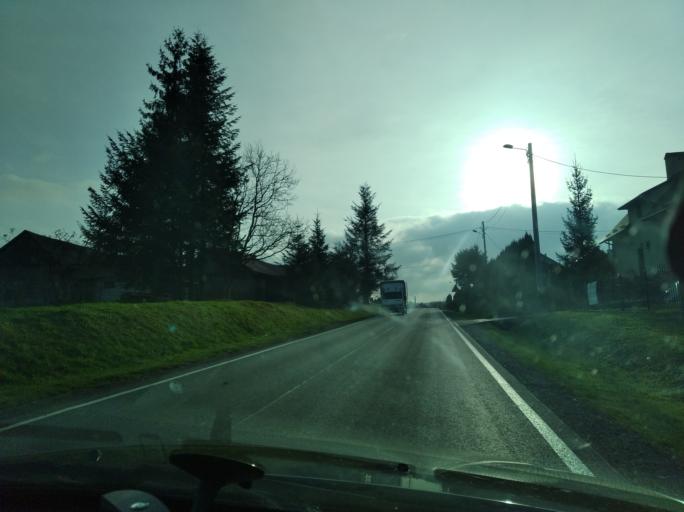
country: PL
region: Subcarpathian Voivodeship
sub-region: Powiat przeworski
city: Siedleczka
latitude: 49.9580
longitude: 22.3928
